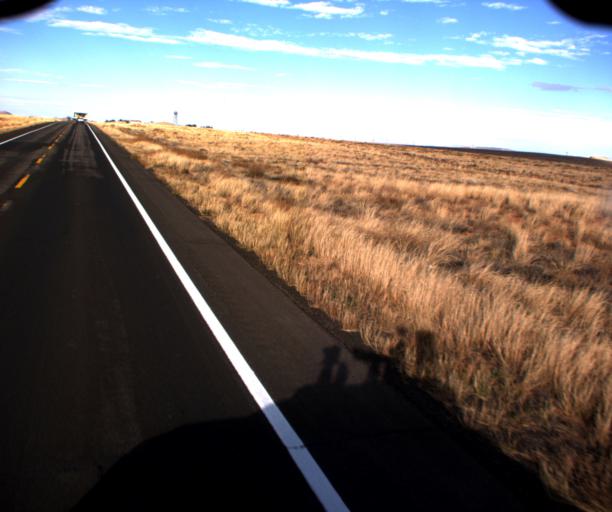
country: US
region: Arizona
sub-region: Apache County
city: Lukachukai
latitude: 36.9603
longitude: -109.3661
